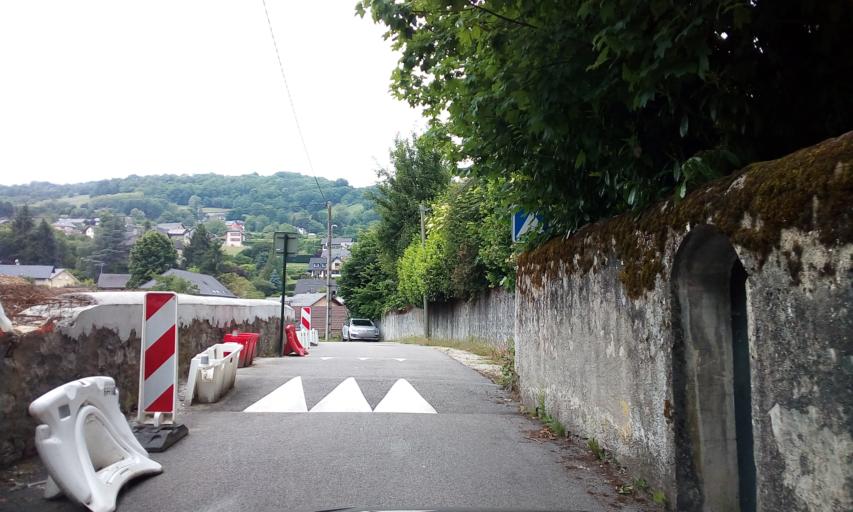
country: FR
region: Rhone-Alpes
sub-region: Departement de la Savoie
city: Barberaz
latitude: 45.5534
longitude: 5.9437
